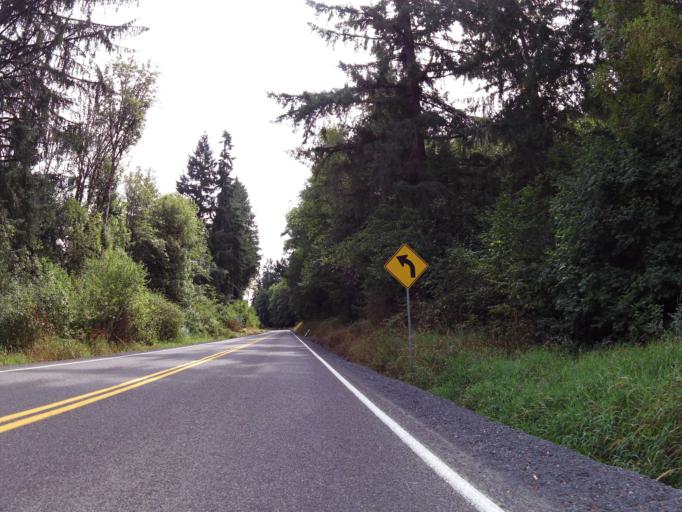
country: US
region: Washington
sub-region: Lewis County
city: Napavine
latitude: 46.5458
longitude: -122.9536
